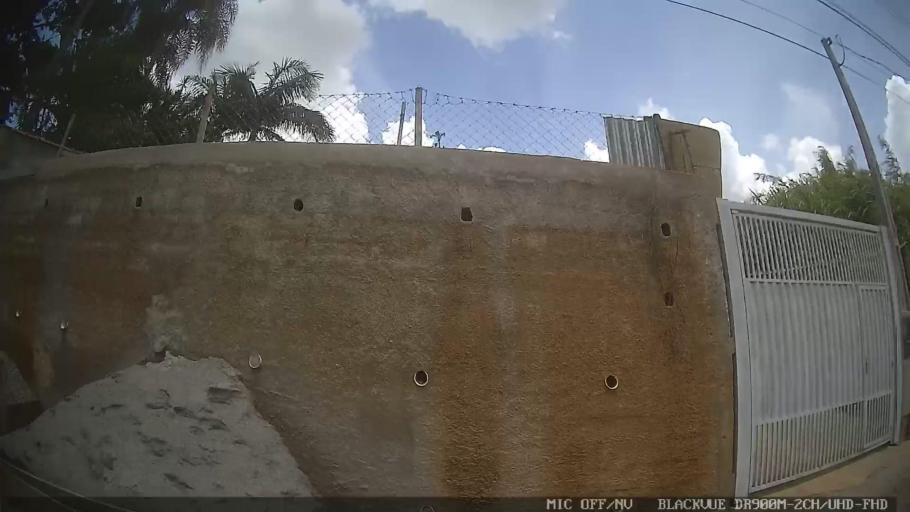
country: BR
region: Sao Paulo
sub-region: Atibaia
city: Atibaia
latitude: -23.0356
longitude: -46.5346
